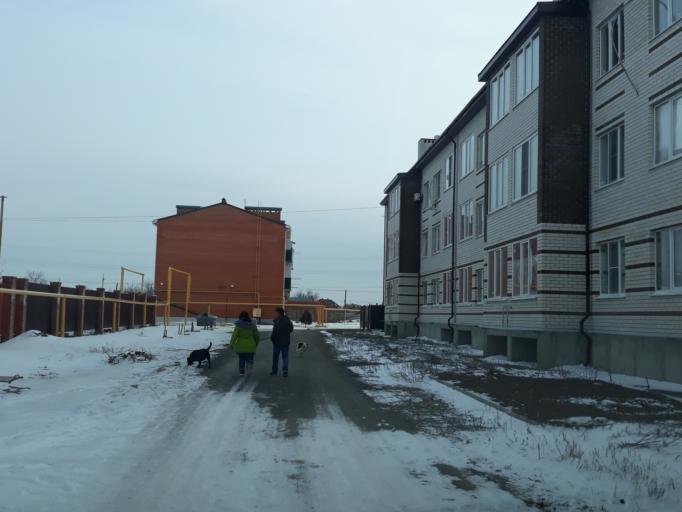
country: RU
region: Rostov
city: Novobessergenovka
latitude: 47.2248
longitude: 38.8408
